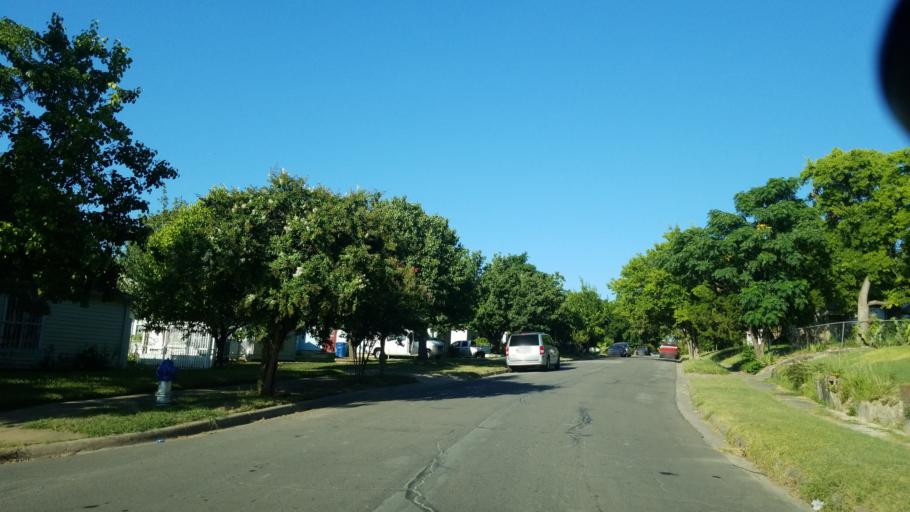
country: US
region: Texas
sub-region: Dallas County
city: Dallas
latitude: 32.7782
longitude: -96.7155
